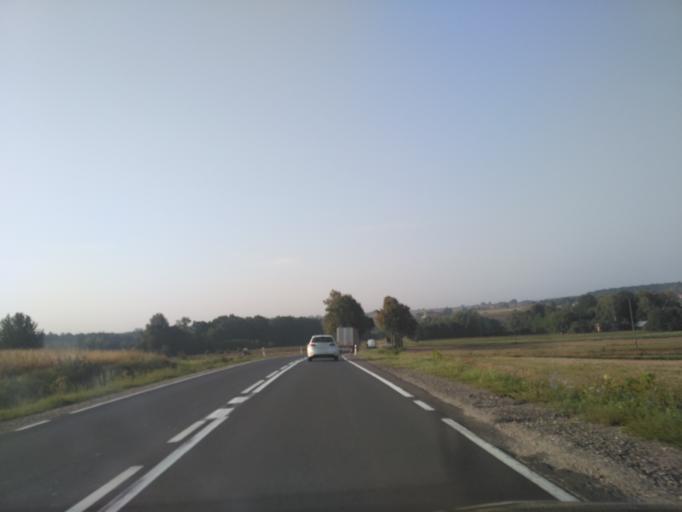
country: PL
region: Lublin Voivodeship
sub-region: Powiat krasnicki
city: Szastarka
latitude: 50.8061
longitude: 22.3198
